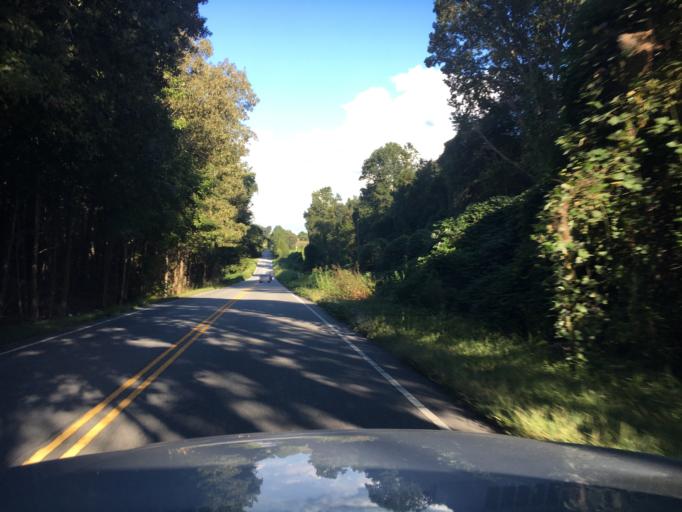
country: US
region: South Carolina
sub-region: Spartanburg County
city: Woodruff
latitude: 34.7909
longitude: -82.1241
